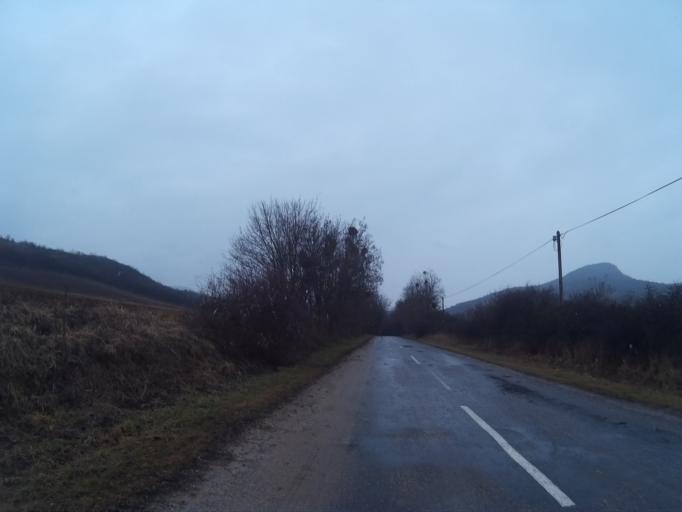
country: HU
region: Komarom-Esztergom
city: Nyergesujfalu
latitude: 47.7101
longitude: 18.5795
